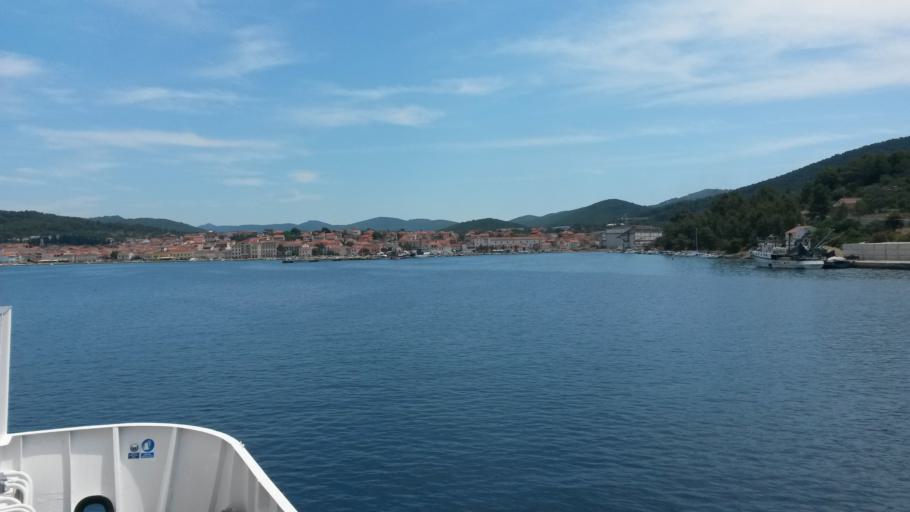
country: HR
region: Dubrovacko-Neretvanska
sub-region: Grad Dubrovnik
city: Vela Luka
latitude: 42.9611
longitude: 16.7035
